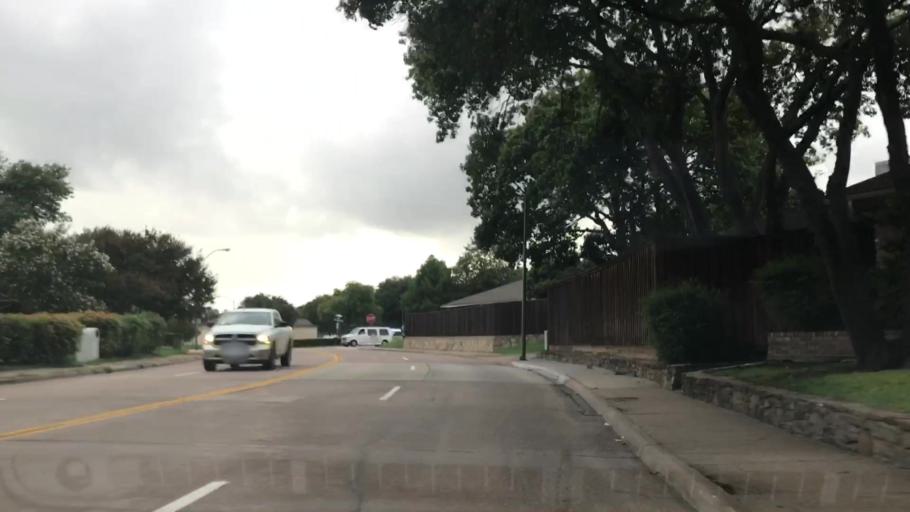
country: US
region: Texas
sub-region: Dallas County
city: Richardson
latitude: 32.9015
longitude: -96.7318
